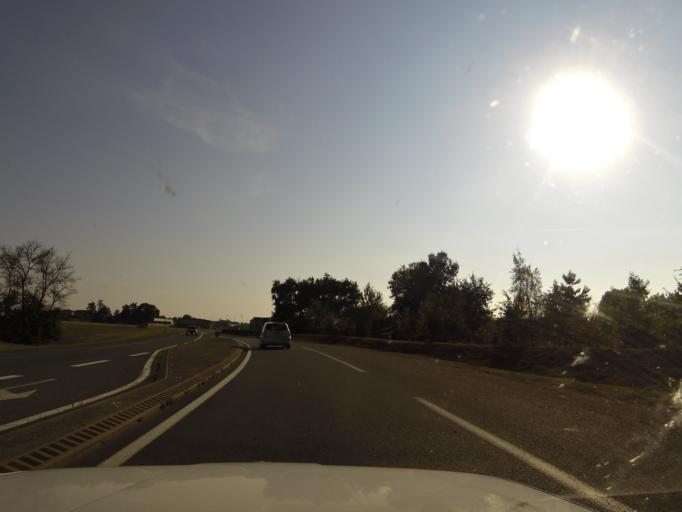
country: FR
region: Rhone-Alpes
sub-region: Departement de l'Ain
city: Meximieux
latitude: 45.9050
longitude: 5.2044
